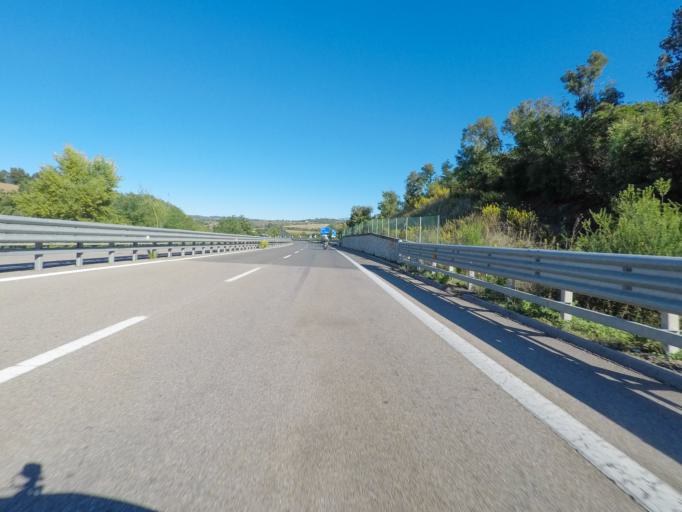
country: IT
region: Tuscany
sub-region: Provincia di Grosseto
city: Campagnatico
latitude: 42.8868
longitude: 11.2299
